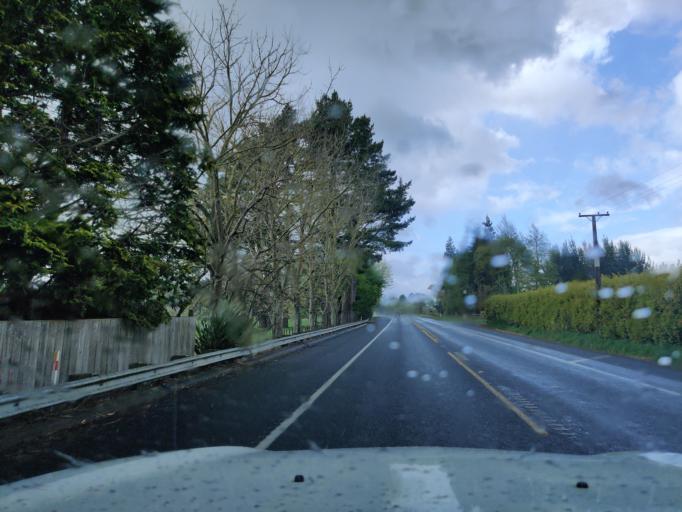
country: NZ
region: Waikato
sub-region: Waipa District
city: Cambridge
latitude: -37.9359
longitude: 175.5749
